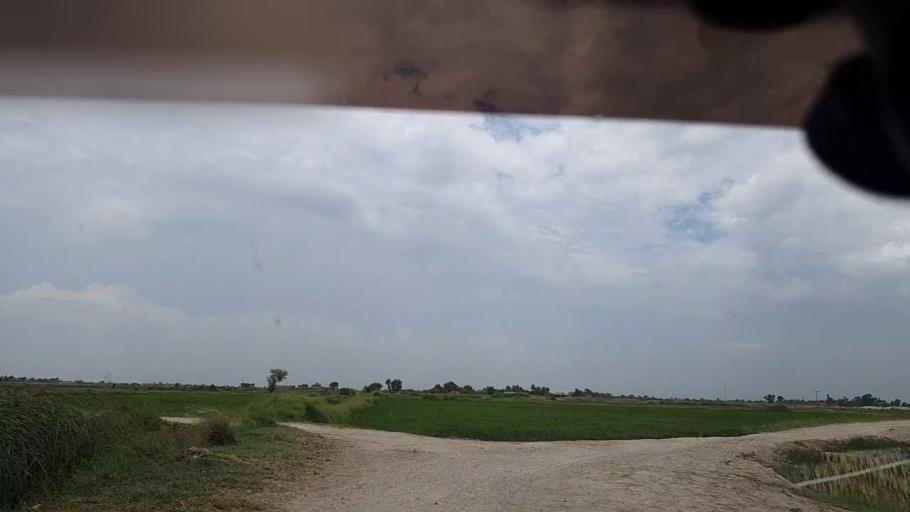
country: PK
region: Sindh
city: Ghauspur
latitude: 28.1134
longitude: 68.9853
